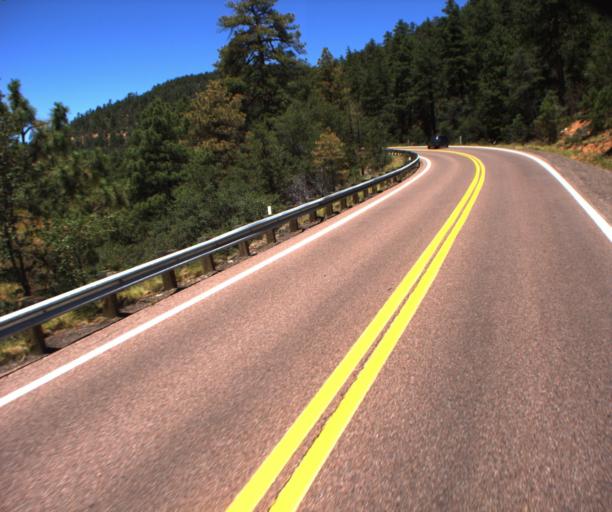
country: US
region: Arizona
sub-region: Gila County
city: Pine
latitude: 34.4162
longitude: -111.4978
